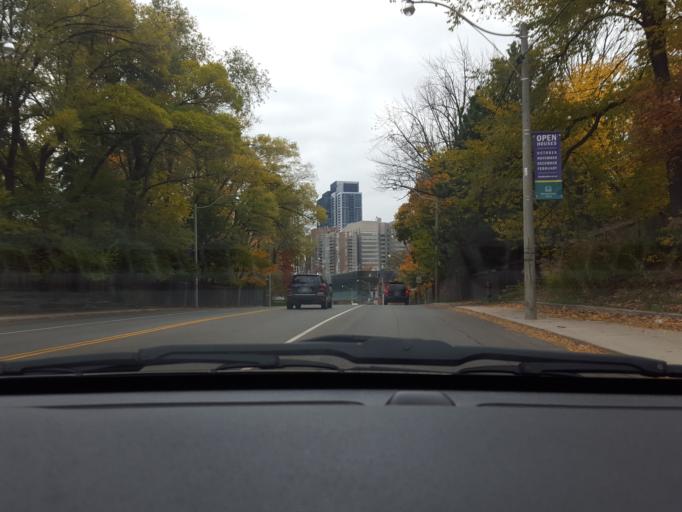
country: CA
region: Ontario
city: Toronto
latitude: 43.6774
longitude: -79.3807
